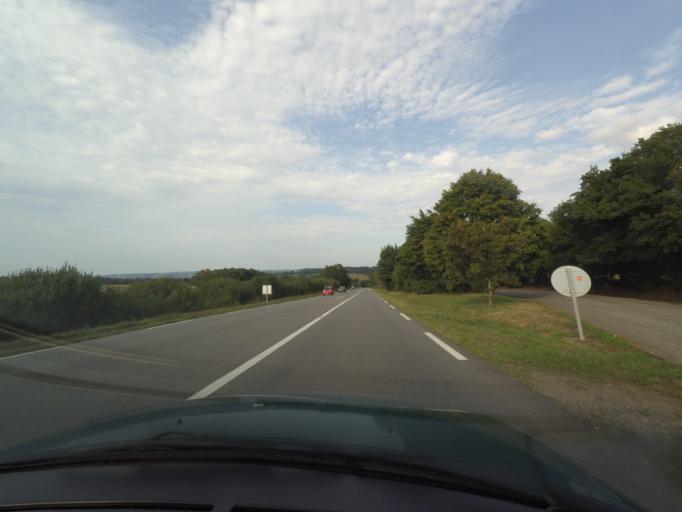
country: FR
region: Limousin
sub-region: Departement de la Haute-Vienne
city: Sereilhac
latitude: 45.7806
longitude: 1.1016
